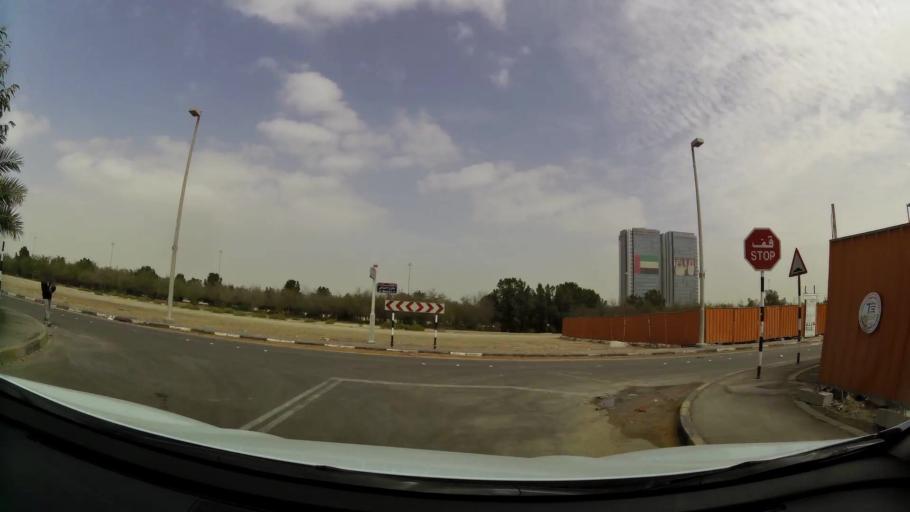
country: AE
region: Abu Dhabi
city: Abu Dhabi
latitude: 24.3932
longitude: 54.5148
